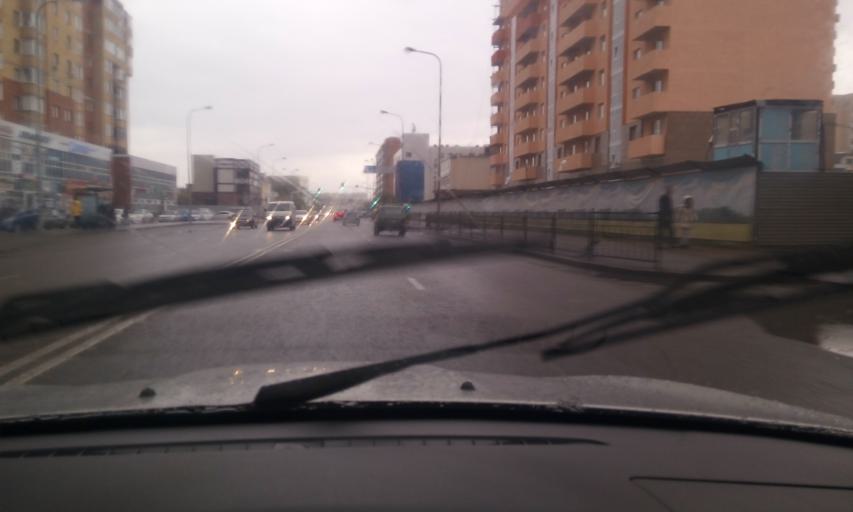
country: KZ
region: Astana Qalasy
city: Astana
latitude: 51.1617
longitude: 71.4569
